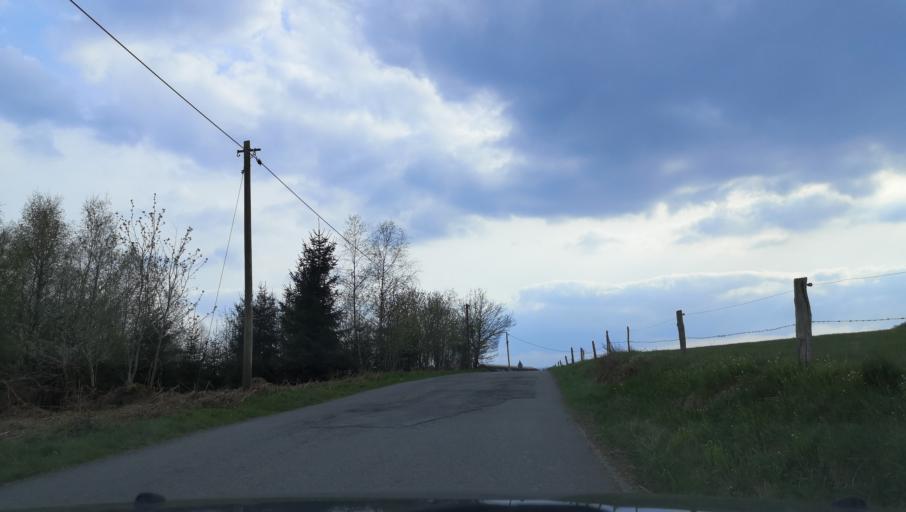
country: DE
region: North Rhine-Westphalia
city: Radevormwald
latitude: 51.2256
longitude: 7.4041
